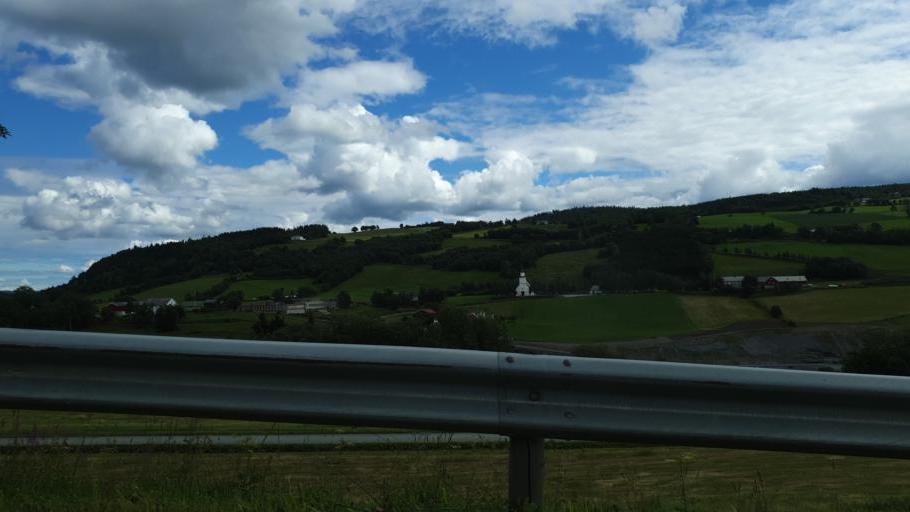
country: NO
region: Sor-Trondelag
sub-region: Midtre Gauldal
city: Storen
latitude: 62.9527
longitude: 10.1805
